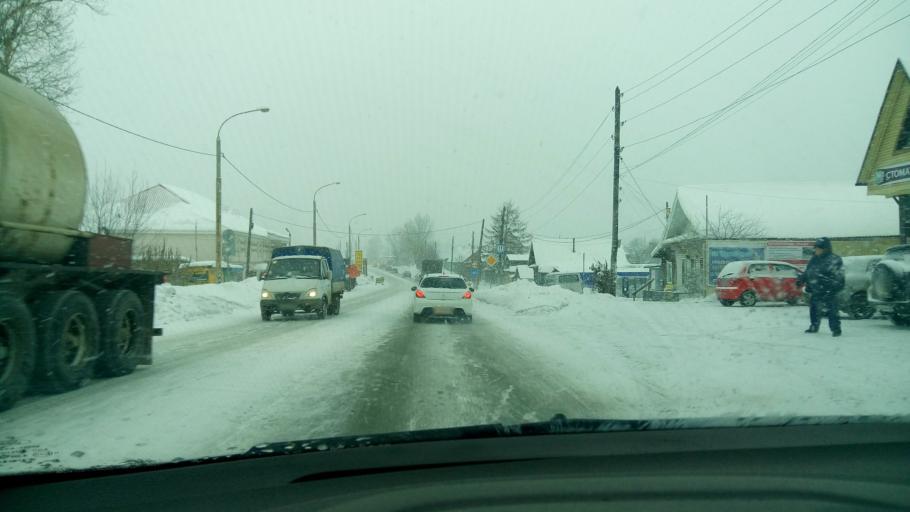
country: RU
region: Sverdlovsk
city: Beloyarskiy
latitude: 56.7625
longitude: 61.4176
